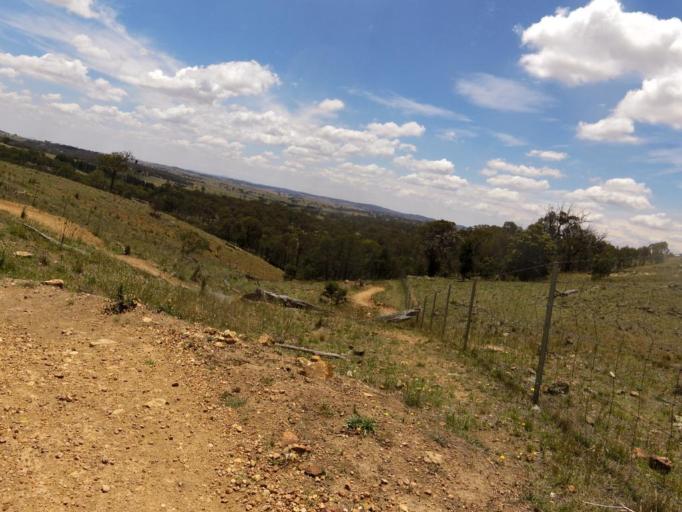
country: AU
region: Australian Capital Territory
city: Kaleen
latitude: -35.1422
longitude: 149.1471
